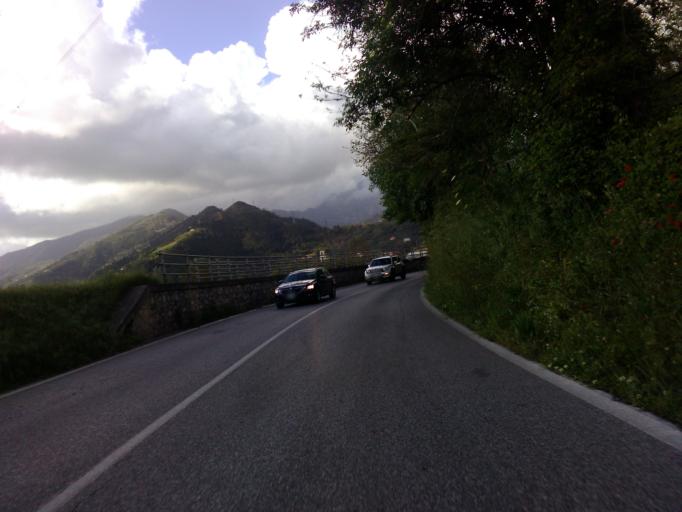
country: IT
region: Tuscany
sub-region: Provincia di Lucca
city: Ripa-Pozzi-Querceta-Ponterosso
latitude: 43.9760
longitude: 10.2201
